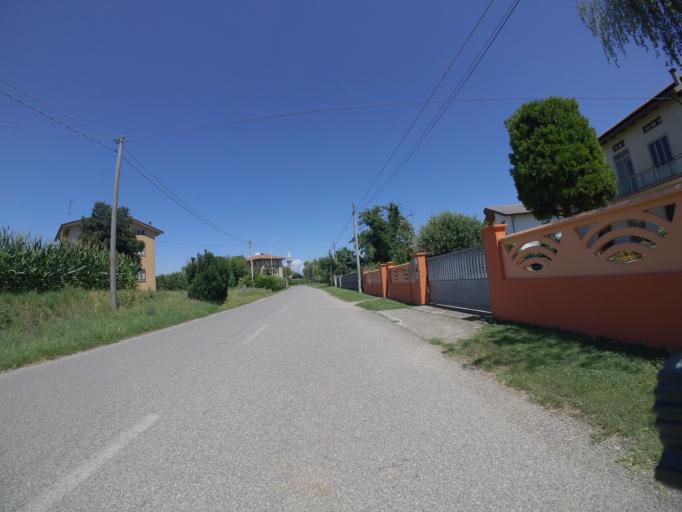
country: IT
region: Friuli Venezia Giulia
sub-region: Provincia di Udine
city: Talmassons
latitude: 45.9250
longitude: 13.1143
